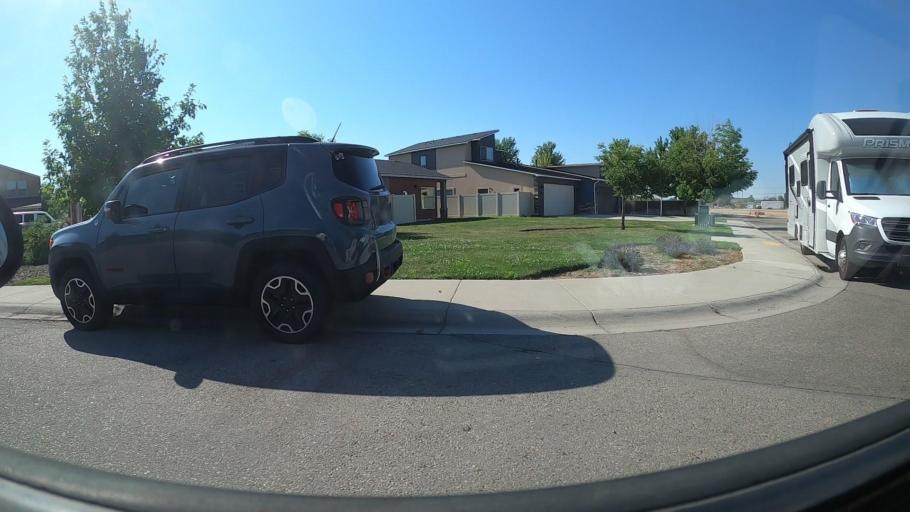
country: US
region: Idaho
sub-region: Ada County
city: Meridian
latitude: 43.6316
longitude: -116.3562
